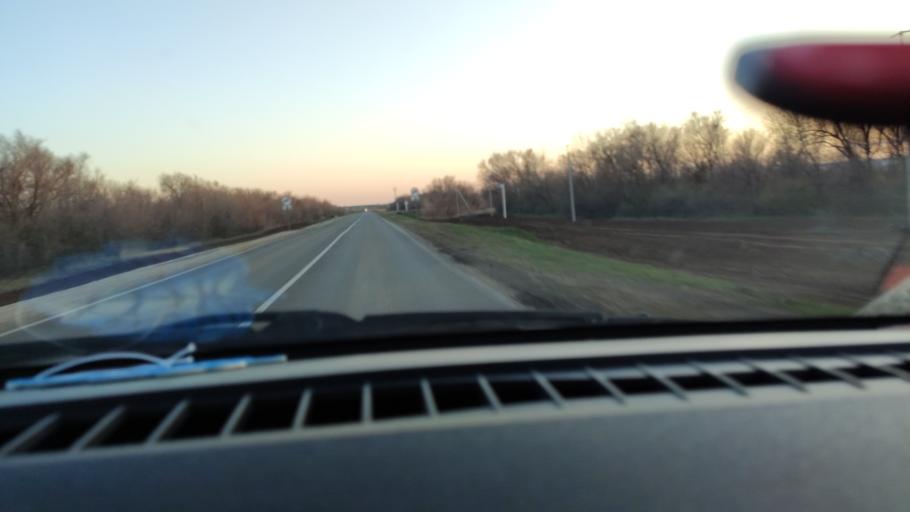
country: RU
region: Saratov
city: Privolzhskiy
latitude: 51.3176
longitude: 46.0212
